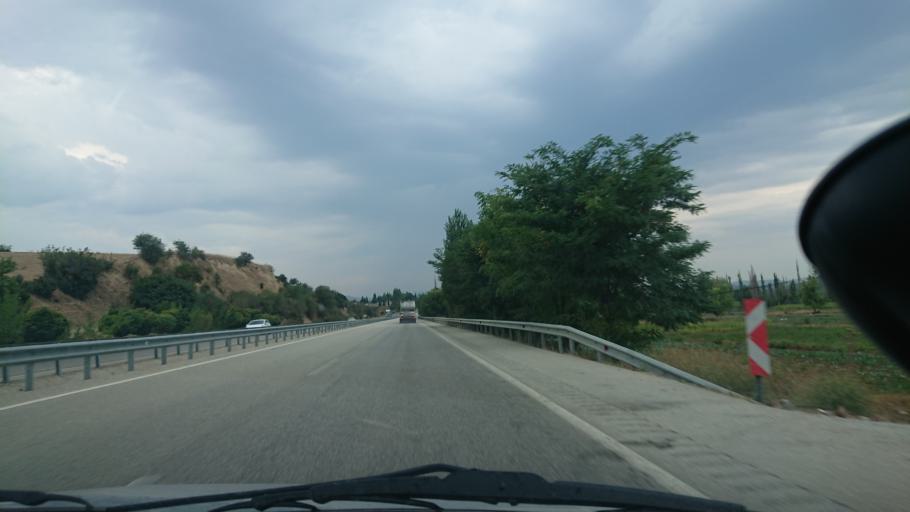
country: TR
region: Manisa
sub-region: Kula
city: Kula
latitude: 38.5893
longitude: 28.7983
